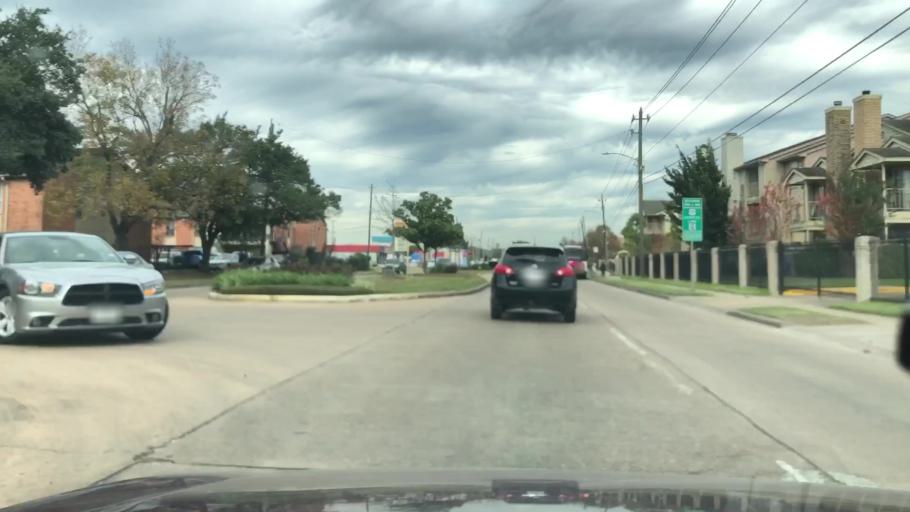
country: US
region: Texas
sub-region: Fort Bend County
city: Missouri City
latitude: 29.6687
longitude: -95.5281
